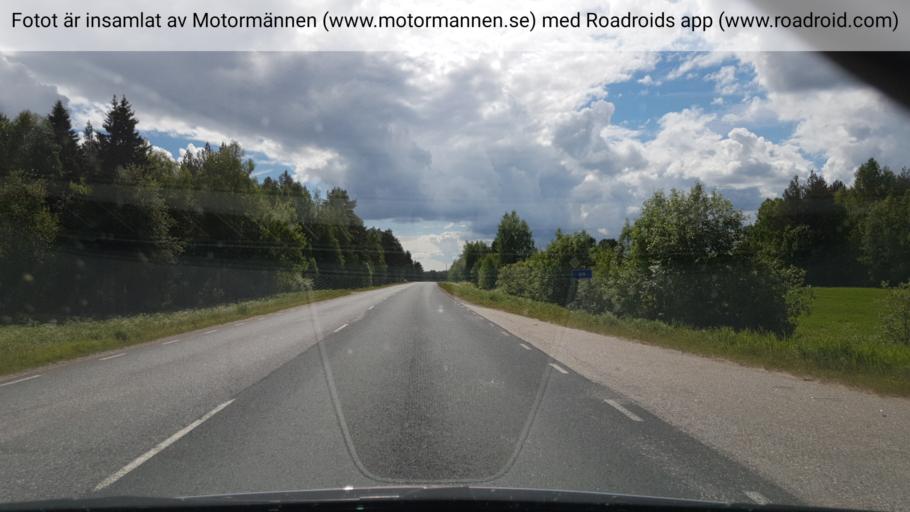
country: FI
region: Lapland
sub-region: Torniolaakso
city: Ylitornio
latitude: 66.2940
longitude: 23.6392
